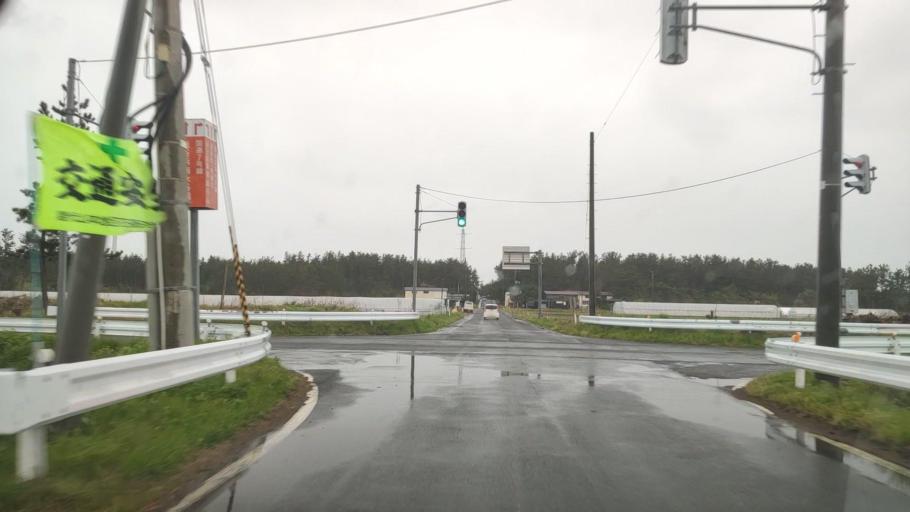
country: JP
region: Akita
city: Noshiromachi
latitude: 40.0977
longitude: 139.9673
